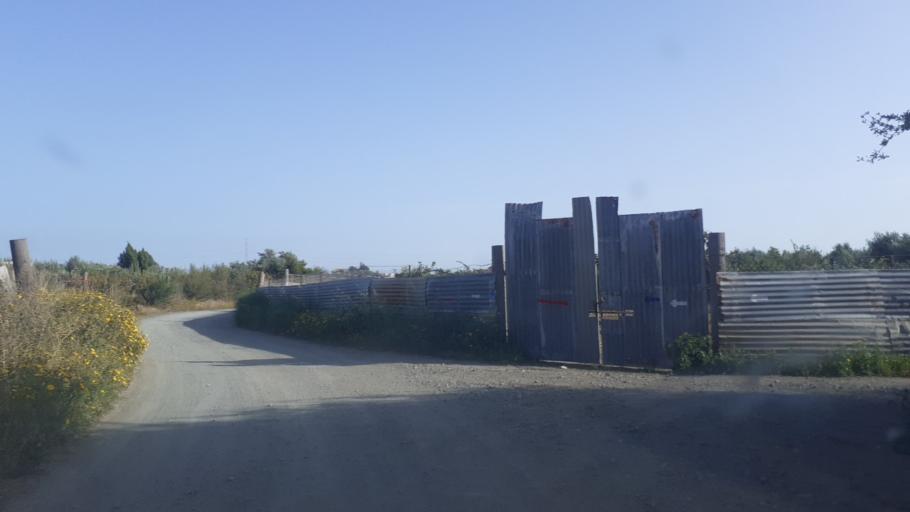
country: CY
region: Larnaka
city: Kolossi
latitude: 34.6673
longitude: 32.9526
